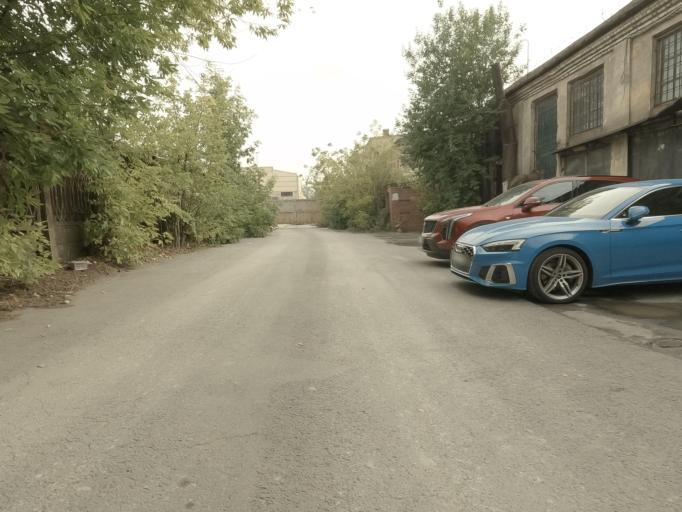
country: RU
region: St.-Petersburg
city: Admiralteisky
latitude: 59.8970
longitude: 30.2924
